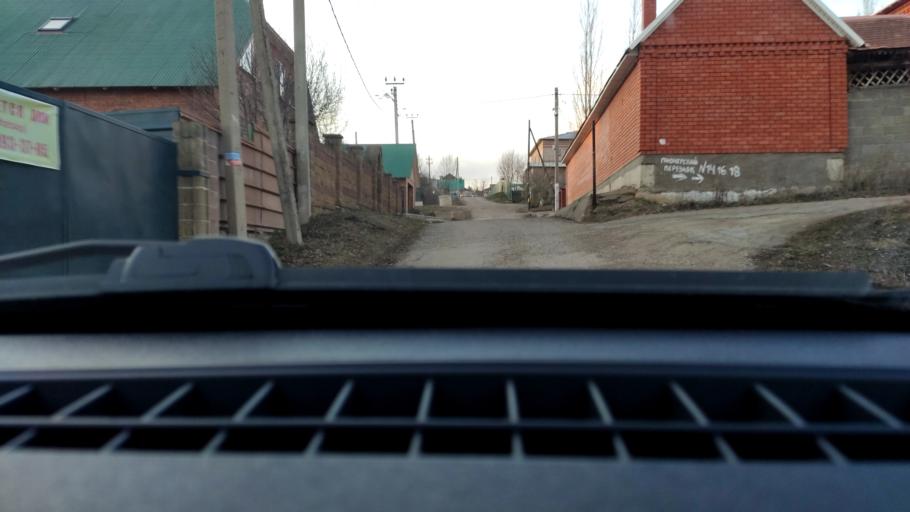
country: RU
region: Bashkortostan
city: Mikhaylovka
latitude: 54.8069
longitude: 55.8858
